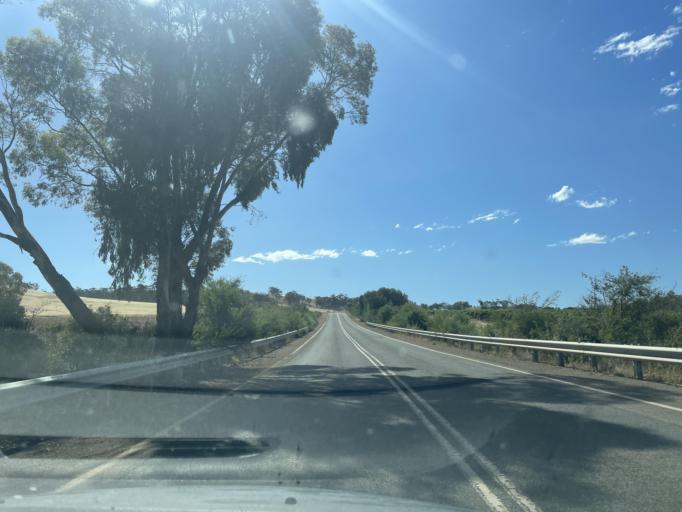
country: AU
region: South Australia
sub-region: Clare and Gilbert Valleys
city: Clare
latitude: -33.9034
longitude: 138.7094
